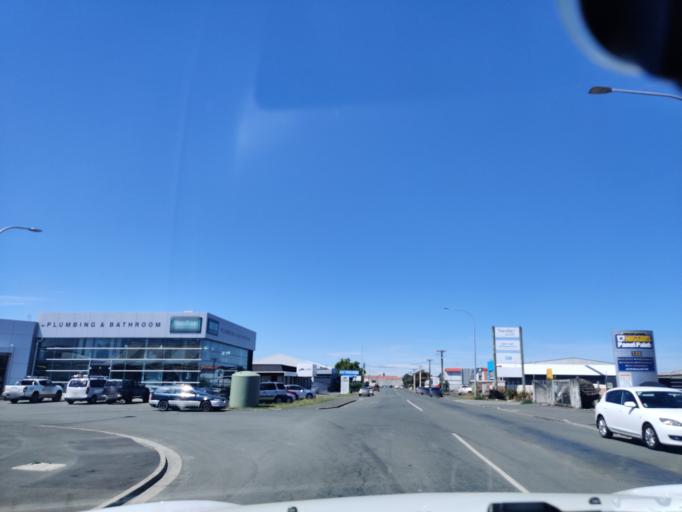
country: NZ
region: Waikato
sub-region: Hamilton City
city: Hamilton
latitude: -37.7962
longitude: 175.2639
